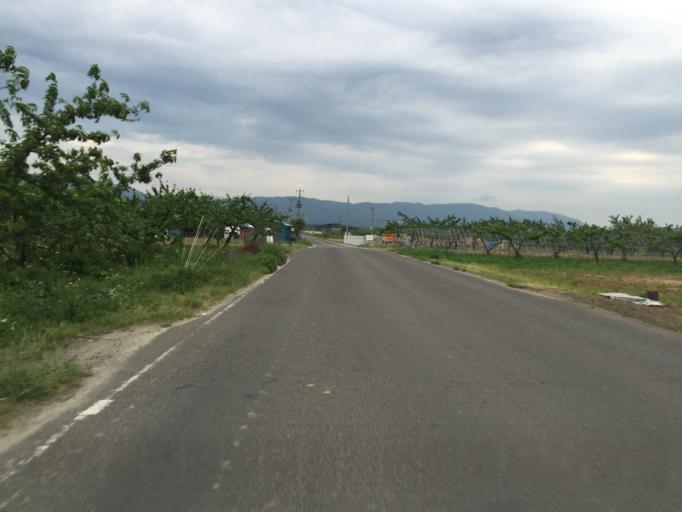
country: JP
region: Fukushima
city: Hobaramachi
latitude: 37.8302
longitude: 140.5382
